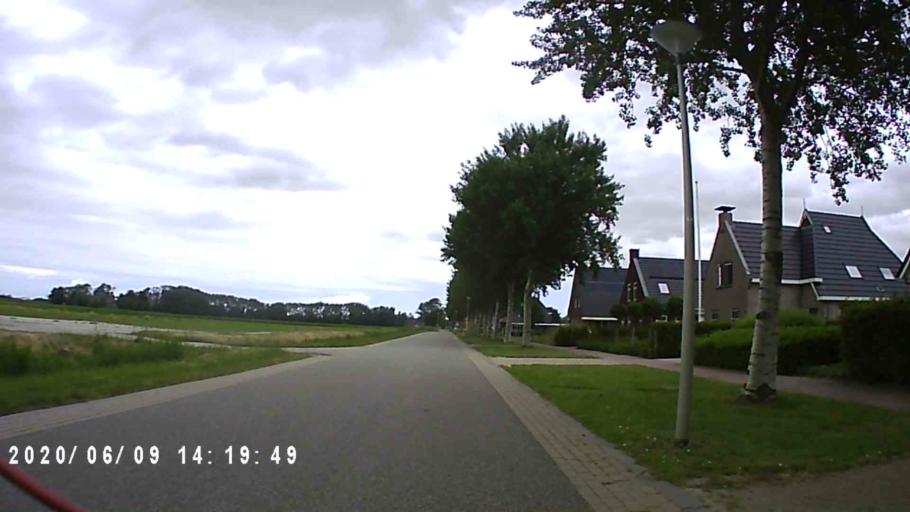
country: NL
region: Groningen
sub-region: Gemeente Bedum
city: Bedum
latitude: 53.2919
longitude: 6.5921
